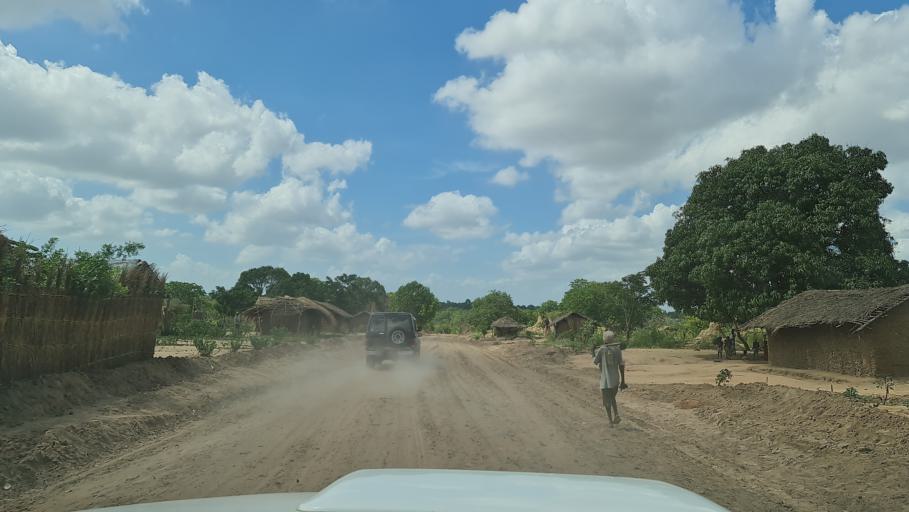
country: MZ
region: Nampula
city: Ilha de Mocambique
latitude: -15.0091
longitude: 40.5609
